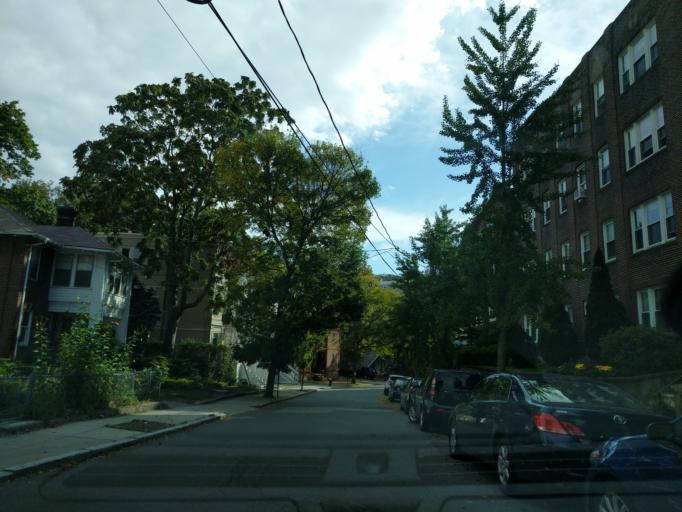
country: US
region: Massachusetts
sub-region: Norfolk County
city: Brookline
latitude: 42.3404
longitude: -71.1462
